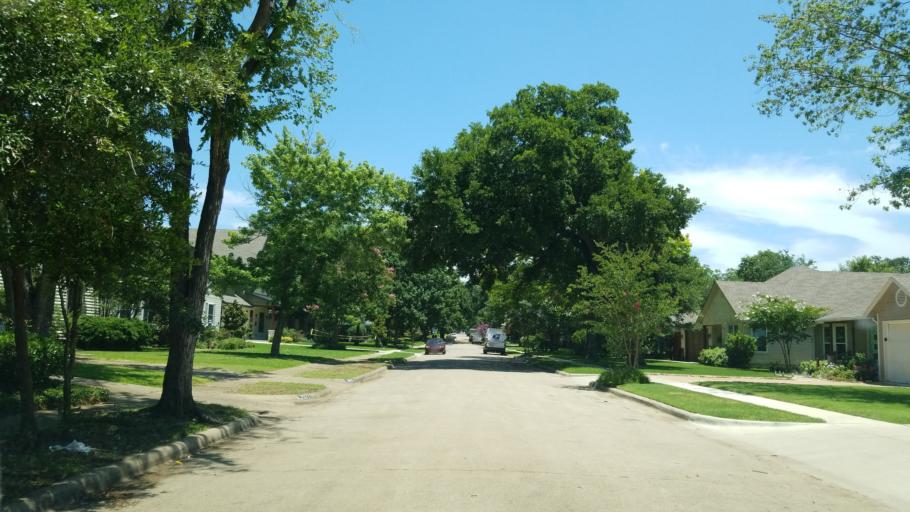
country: US
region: Texas
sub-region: Dallas County
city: University Park
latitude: 32.8762
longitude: -96.8474
